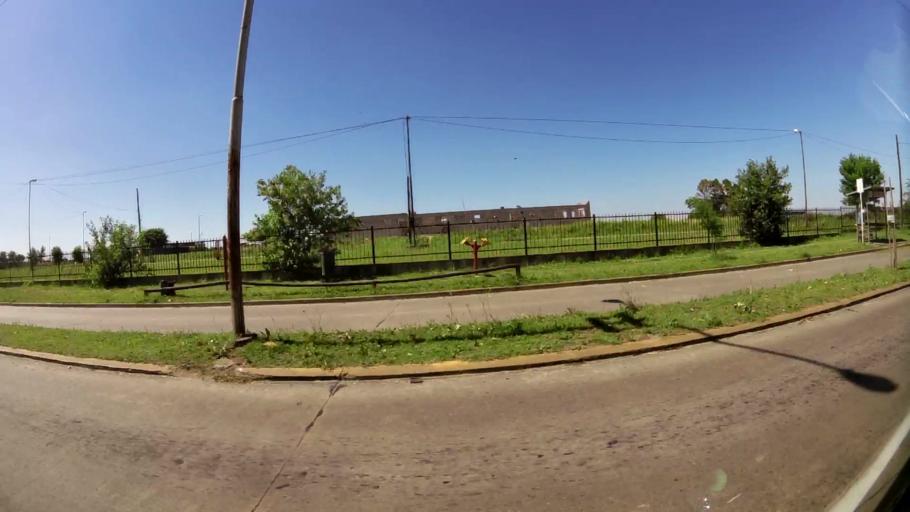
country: AR
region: Buenos Aires
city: Ituzaingo
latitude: -34.6622
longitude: -58.6442
